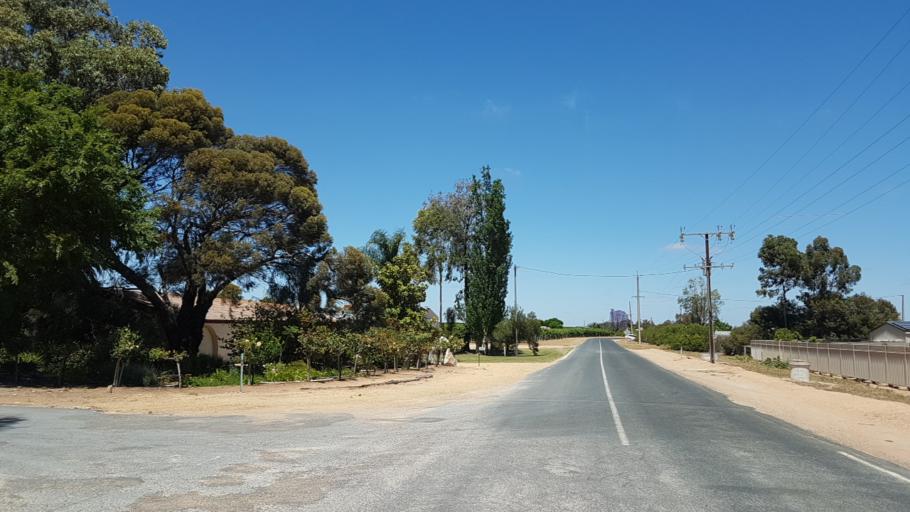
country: AU
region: South Australia
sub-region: Loxton Waikerie
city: Waikerie
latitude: -34.1706
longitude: 140.0323
